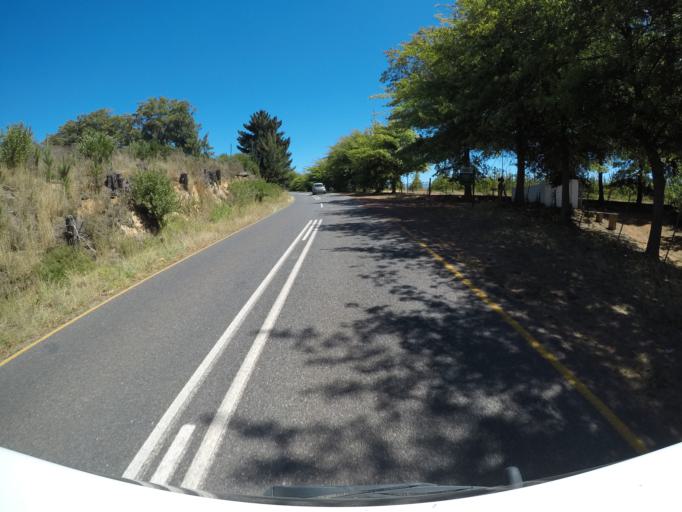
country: ZA
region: Western Cape
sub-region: Overberg District Municipality
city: Grabouw
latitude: -34.2099
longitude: 19.0435
